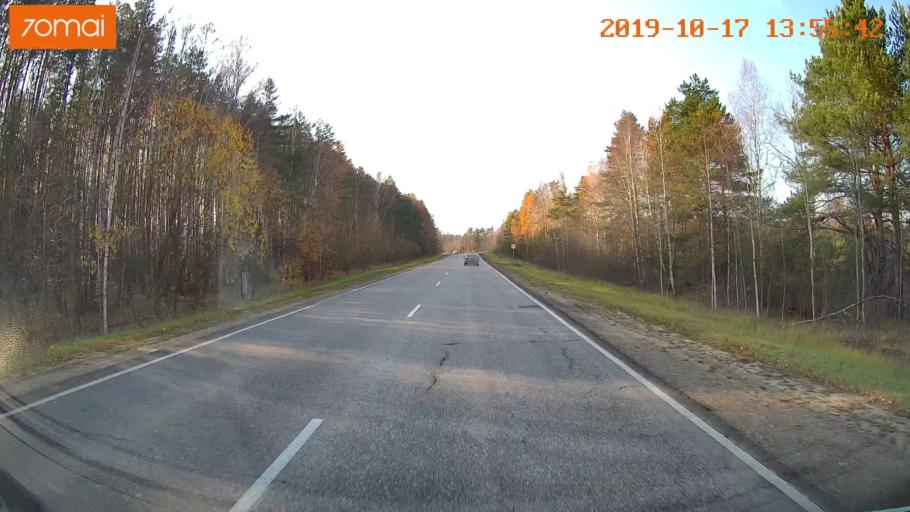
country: RU
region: Rjazan
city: Spas-Klepiki
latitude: 55.1525
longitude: 40.2826
